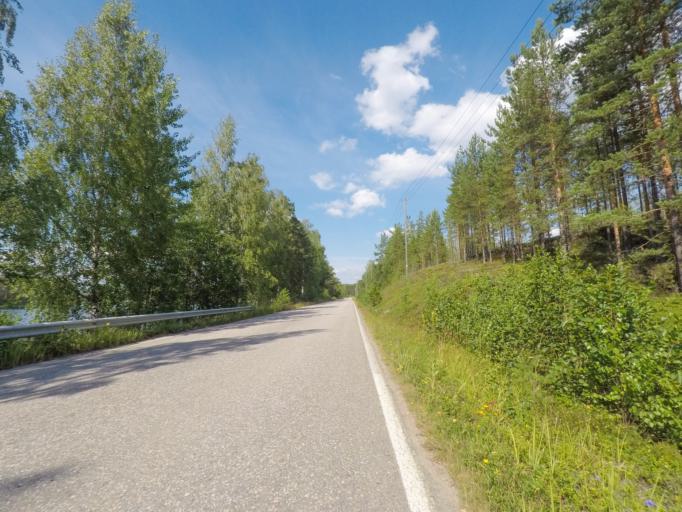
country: FI
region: Southern Savonia
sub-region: Mikkeli
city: Puumala
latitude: 61.4889
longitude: 28.1663
